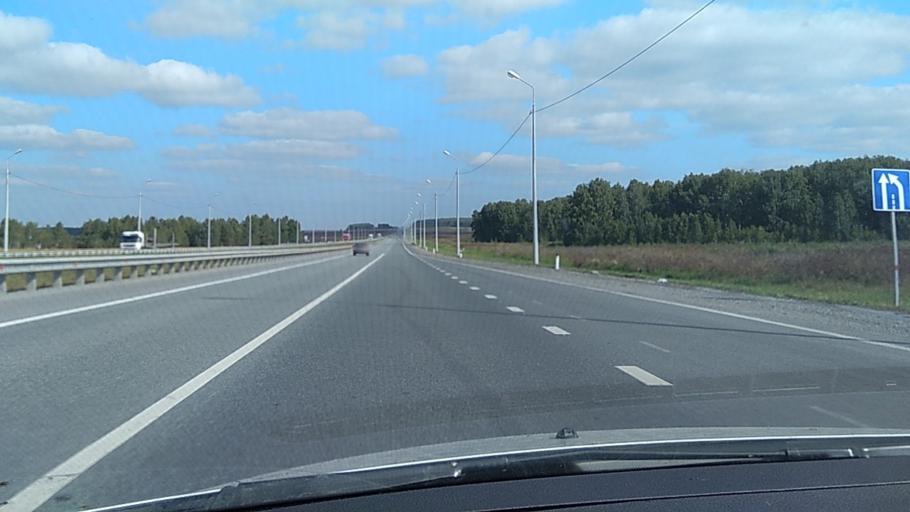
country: RU
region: Chelyabinsk
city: Chebarkul'
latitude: 54.9102
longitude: 60.4400
